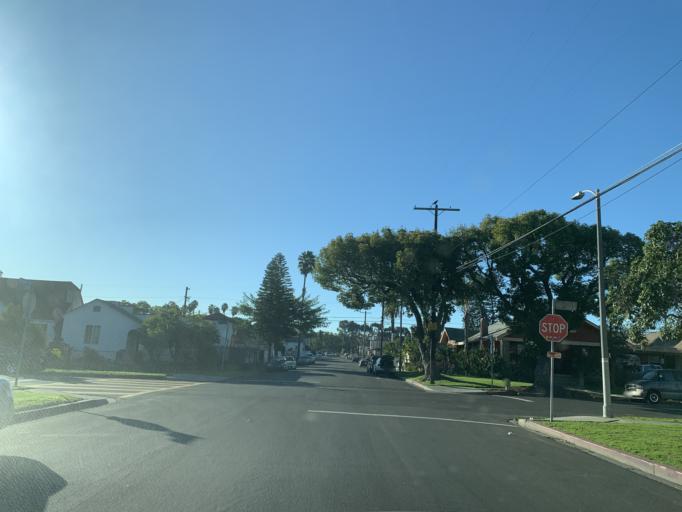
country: US
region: California
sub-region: Los Angeles County
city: Westmont
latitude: 33.9332
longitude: -118.2848
